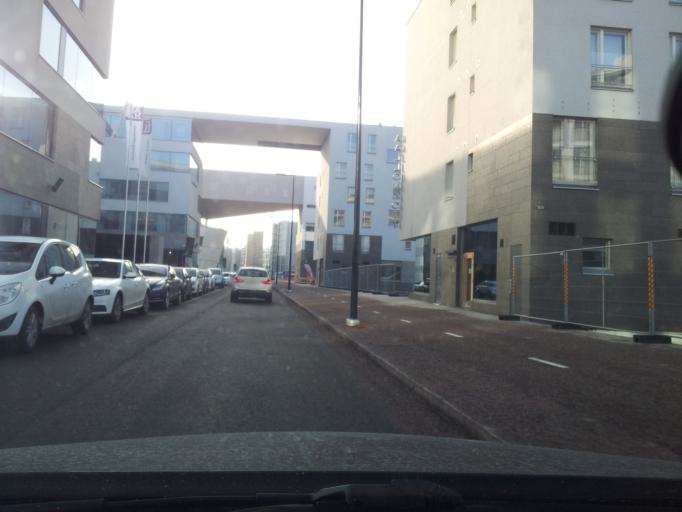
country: FI
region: Uusimaa
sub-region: Helsinki
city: Helsinki
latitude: 60.1764
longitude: 24.9382
